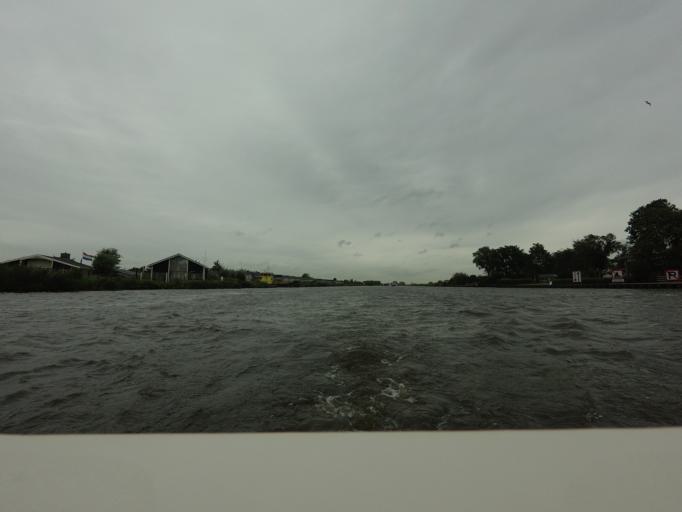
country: NL
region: Friesland
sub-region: Gemeente Boarnsterhim
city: Grou
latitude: 53.0998
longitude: 5.8494
